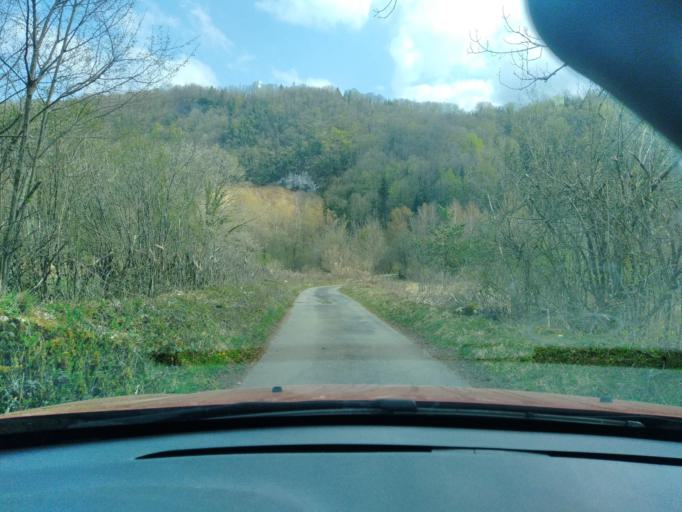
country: FR
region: Franche-Comte
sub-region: Departement du Jura
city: Moirans-en-Montagne
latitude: 46.4543
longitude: 5.7340
